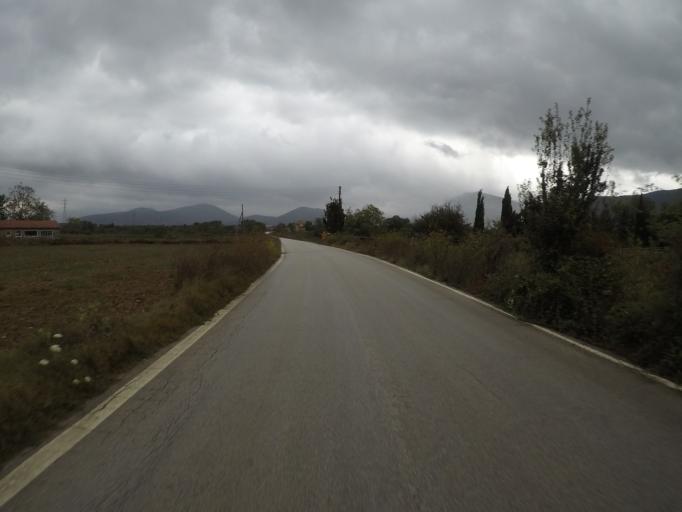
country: GR
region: Peloponnese
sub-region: Nomos Arkadias
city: Tripoli
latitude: 37.5649
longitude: 22.4064
